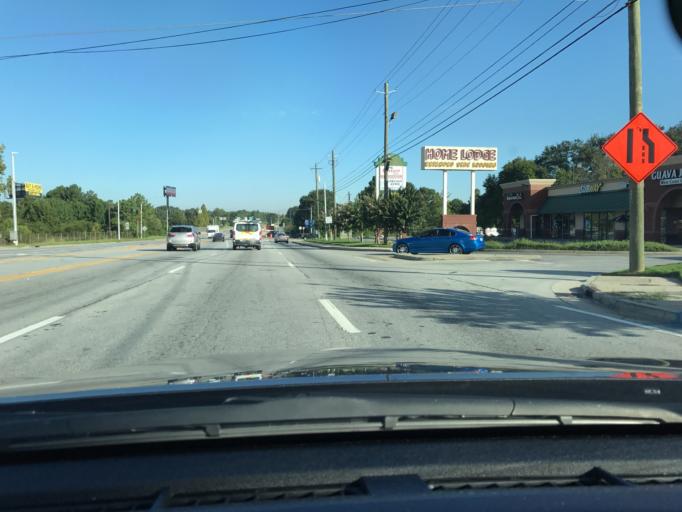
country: US
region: Georgia
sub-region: Clayton County
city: Forest Park
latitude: 33.6302
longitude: -84.3860
